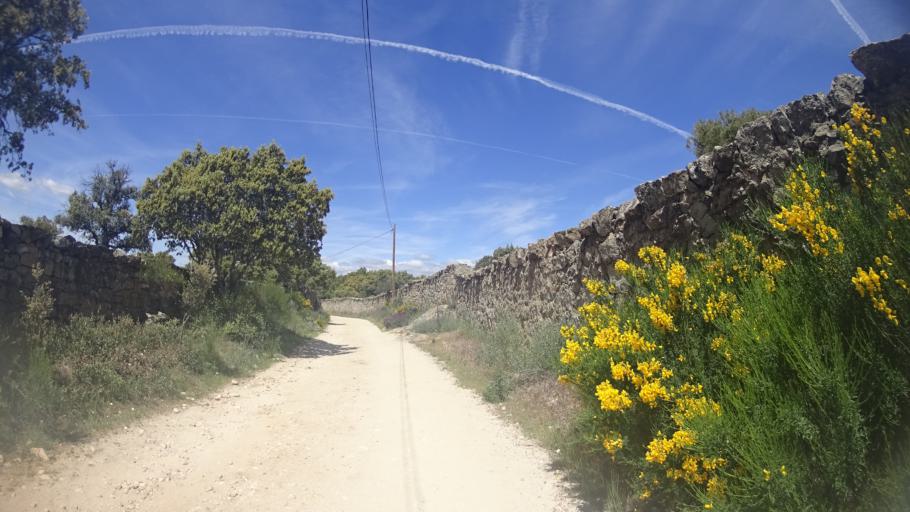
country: ES
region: Madrid
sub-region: Provincia de Madrid
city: Galapagar
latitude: 40.5591
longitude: -3.9858
